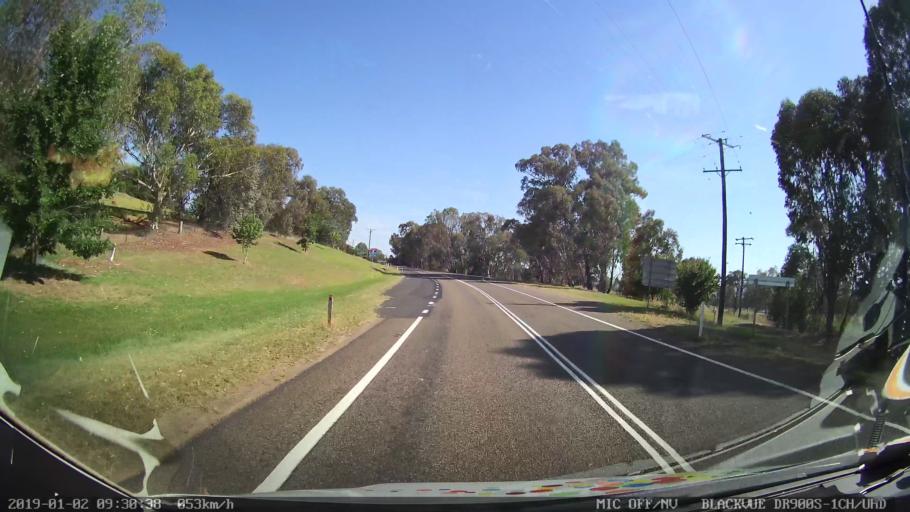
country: AU
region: New South Wales
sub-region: Tumut Shire
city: Tumut
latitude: -35.3249
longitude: 148.2379
